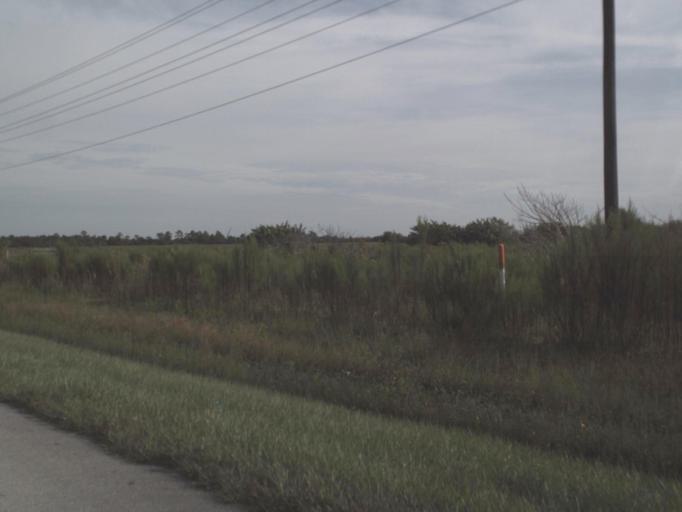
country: US
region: Florida
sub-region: Lee County
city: Fort Myers Shores
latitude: 26.7616
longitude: -81.7608
